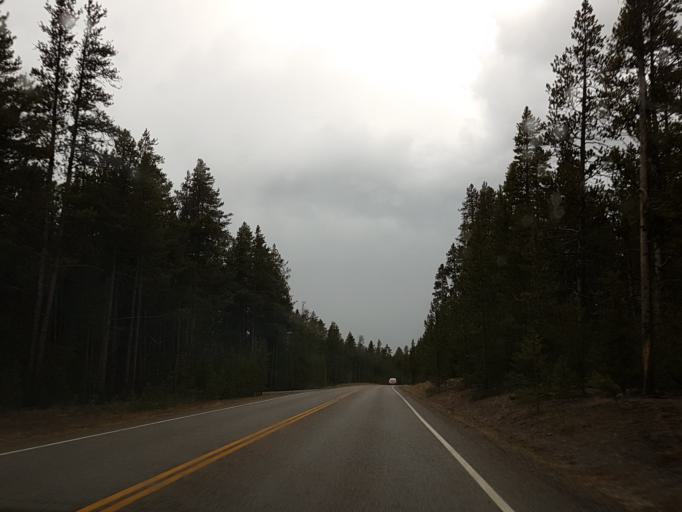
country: US
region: Montana
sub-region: Gallatin County
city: West Yellowstone
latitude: 44.4610
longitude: -110.5110
